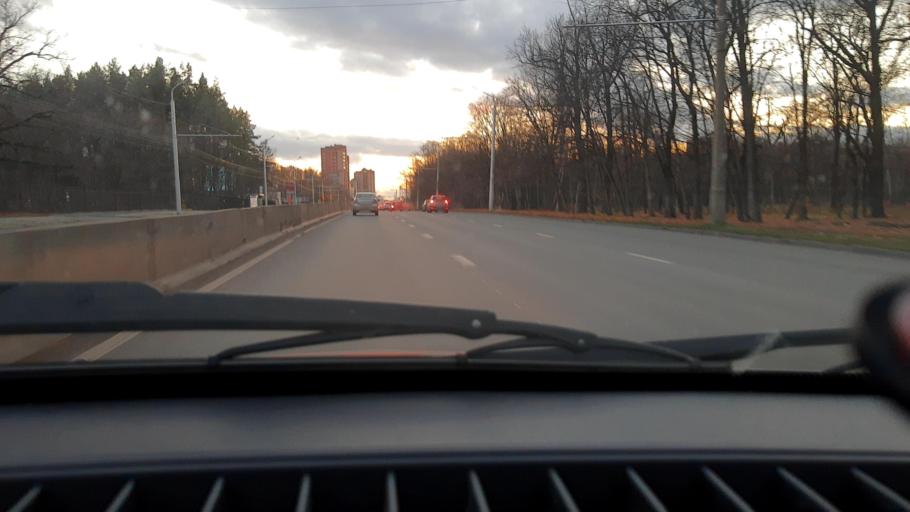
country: RU
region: Bashkortostan
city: Ufa
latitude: 54.7272
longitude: 56.0212
